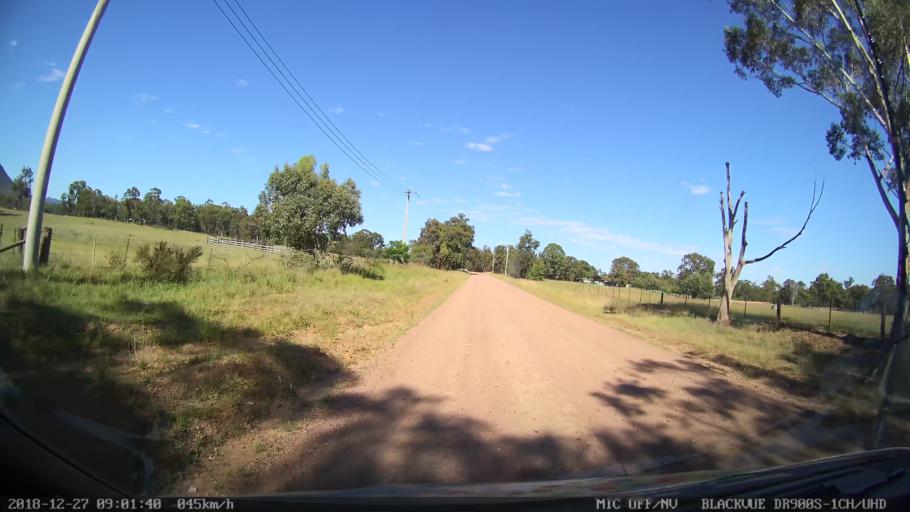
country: AU
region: New South Wales
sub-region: Lithgow
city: Portland
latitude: -33.1017
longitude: 150.2149
